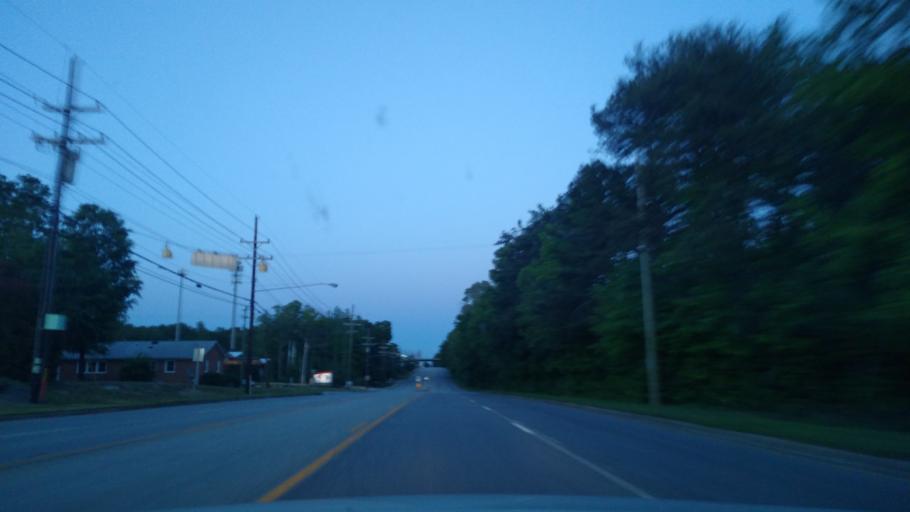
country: US
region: North Carolina
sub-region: Guilford County
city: Oak Ridge
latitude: 36.0933
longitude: -79.9612
